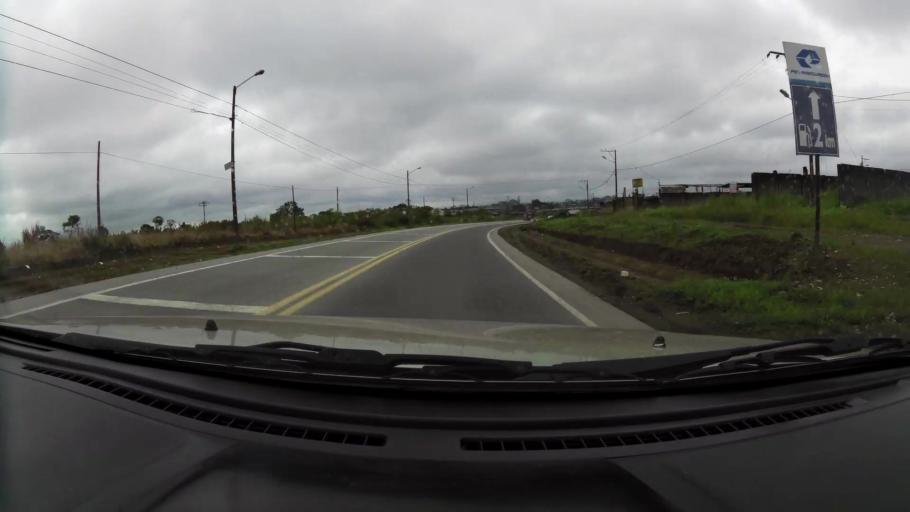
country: EC
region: Santo Domingo de los Tsachilas
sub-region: Canton Santo Domingo de los Colorados
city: Santo Domingo de los Colorados
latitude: -0.2829
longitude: -79.1869
